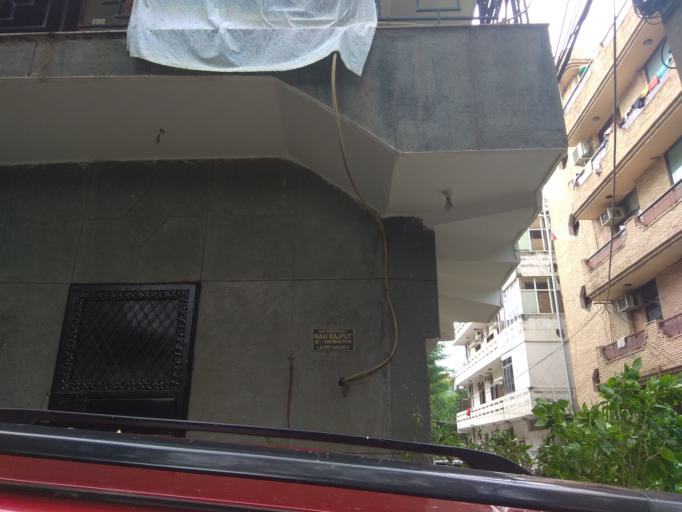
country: IN
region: NCT
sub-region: New Delhi
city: New Delhi
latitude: 28.5669
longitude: 77.2501
